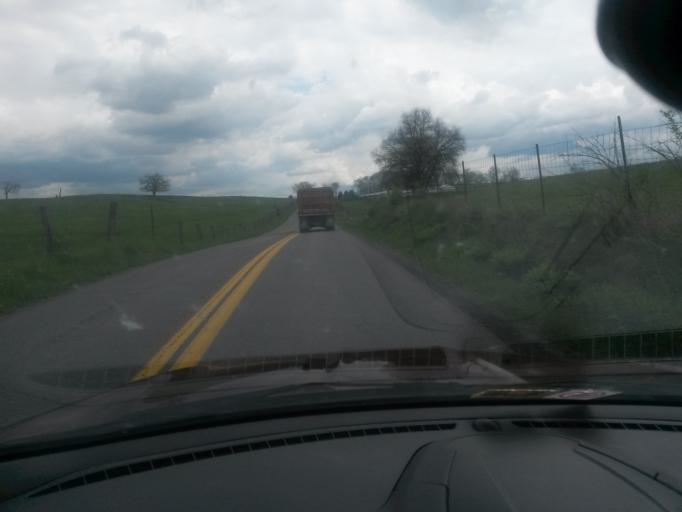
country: US
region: West Virginia
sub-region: Greenbrier County
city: Lewisburg
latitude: 37.8927
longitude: -80.4222
